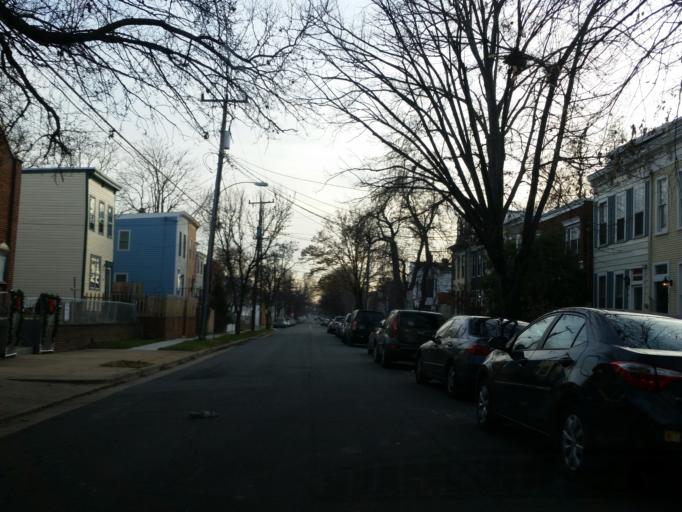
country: US
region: Virginia
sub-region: City of Alexandria
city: Alexandria
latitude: 38.8090
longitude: -77.0529
